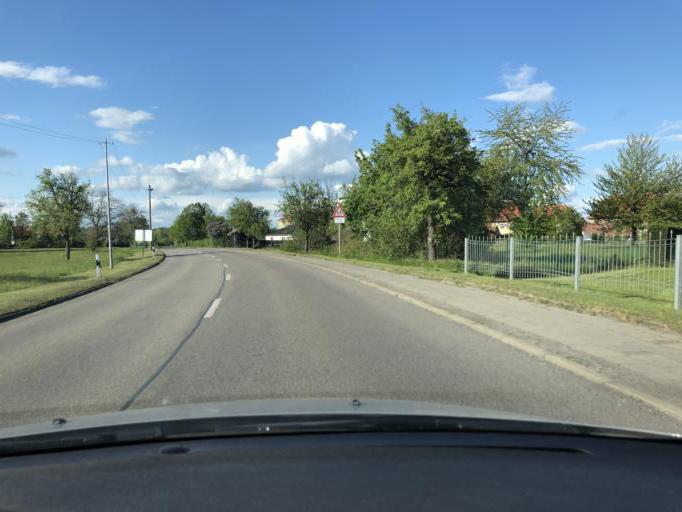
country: DE
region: Saxony
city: Deutzen
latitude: 51.1129
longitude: 12.4297
